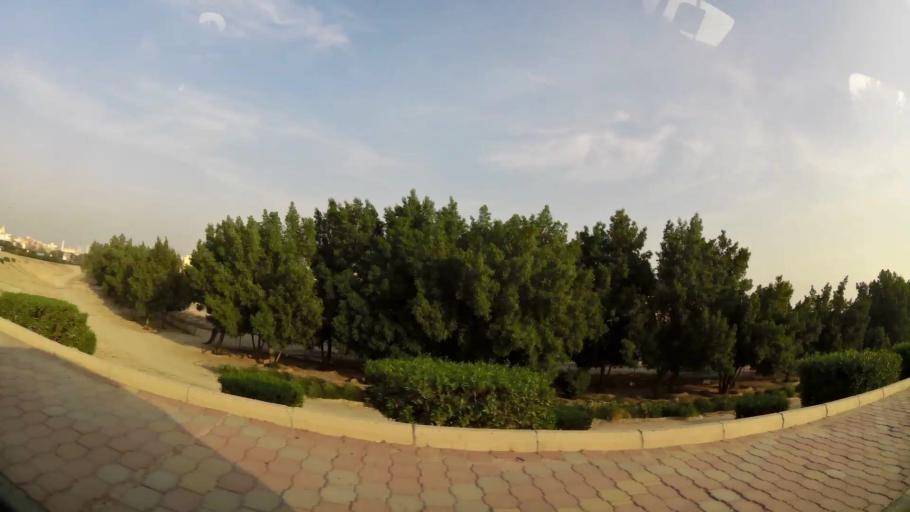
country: KW
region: Mubarak al Kabir
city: Sabah as Salim
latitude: 29.2388
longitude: 48.0514
